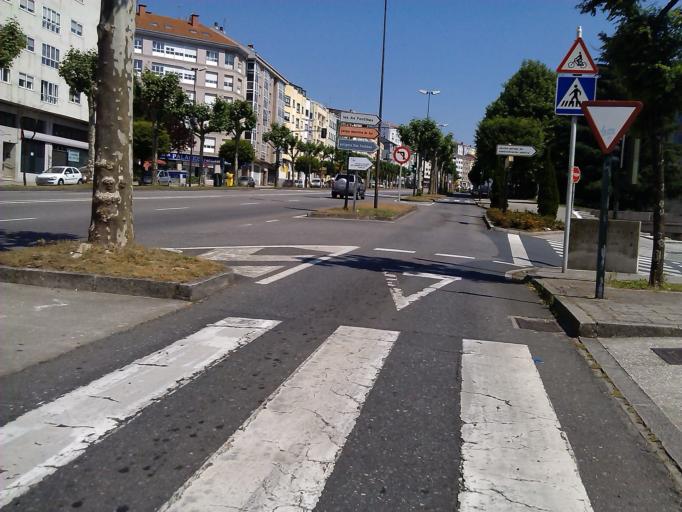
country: ES
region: Galicia
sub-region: Provincia da Coruna
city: Santiago de Compostela
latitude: 42.8820
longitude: -8.5331
